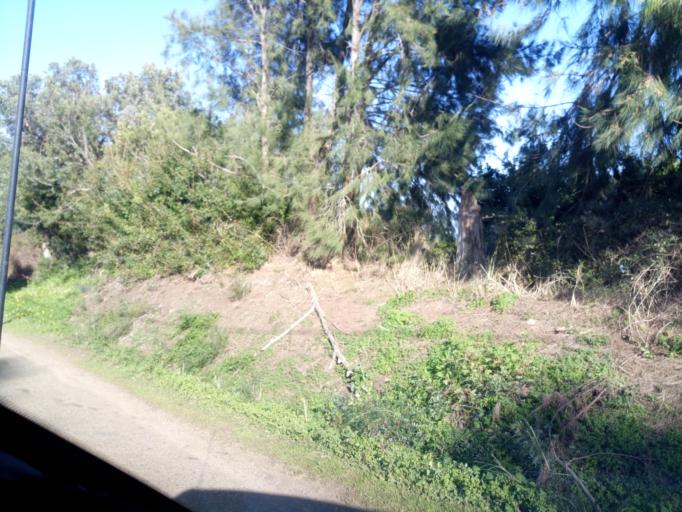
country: FR
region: Corsica
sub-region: Departement de la Haute-Corse
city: Linguizzetta
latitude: 42.2660
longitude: 9.5440
